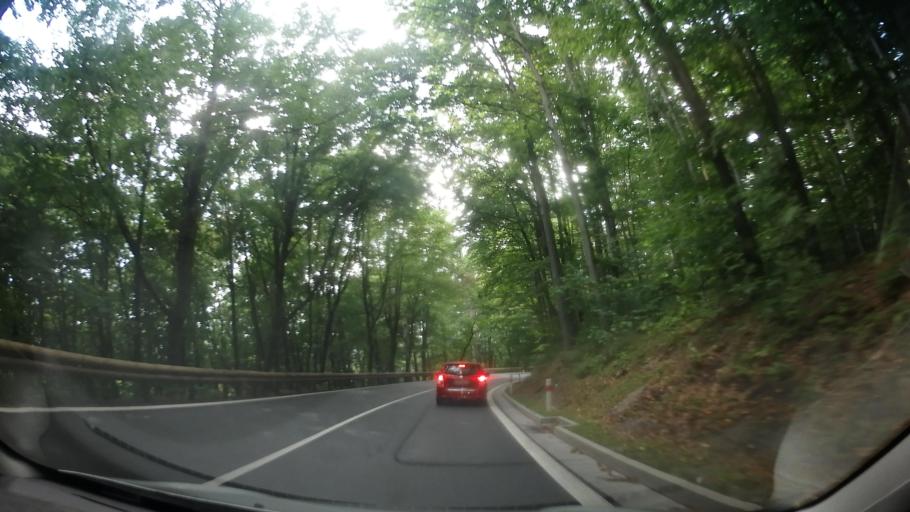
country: CZ
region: Pardubicky
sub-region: Okres Chrudim
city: Tremosnice
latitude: 49.8728
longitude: 15.5863
